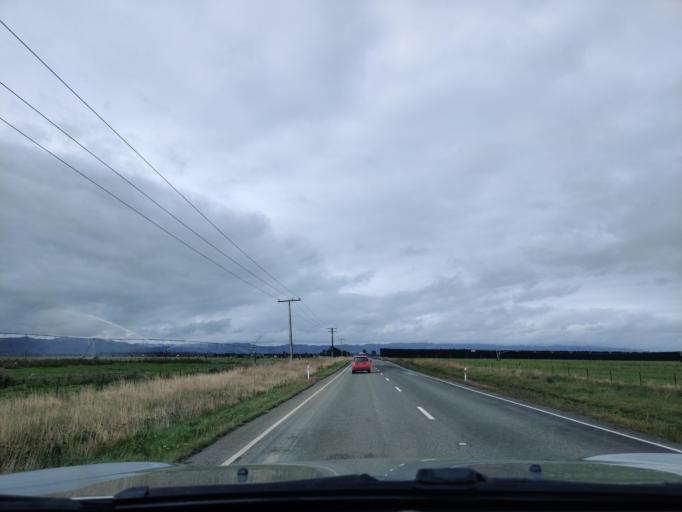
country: NZ
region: Canterbury
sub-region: Hurunui District
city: Amberley
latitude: -42.7317
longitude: 172.8685
